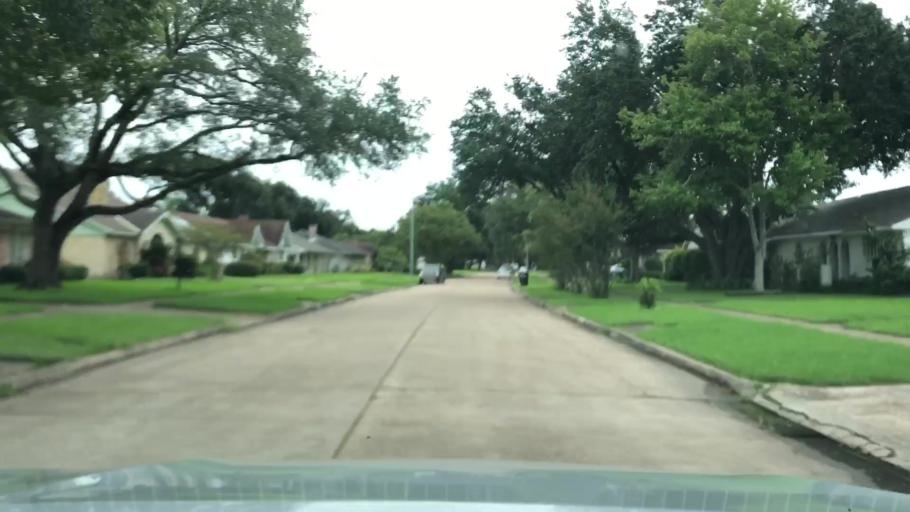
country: US
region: Texas
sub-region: Fort Bend County
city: Meadows Place
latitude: 29.7007
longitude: -95.5491
